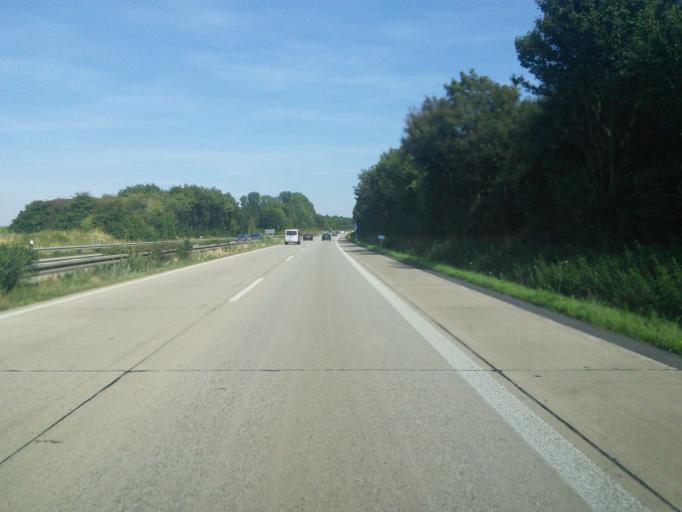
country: DE
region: North Rhine-Westphalia
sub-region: Regierungsbezirk Dusseldorf
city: Schwalmtal
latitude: 51.2111
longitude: 6.3320
